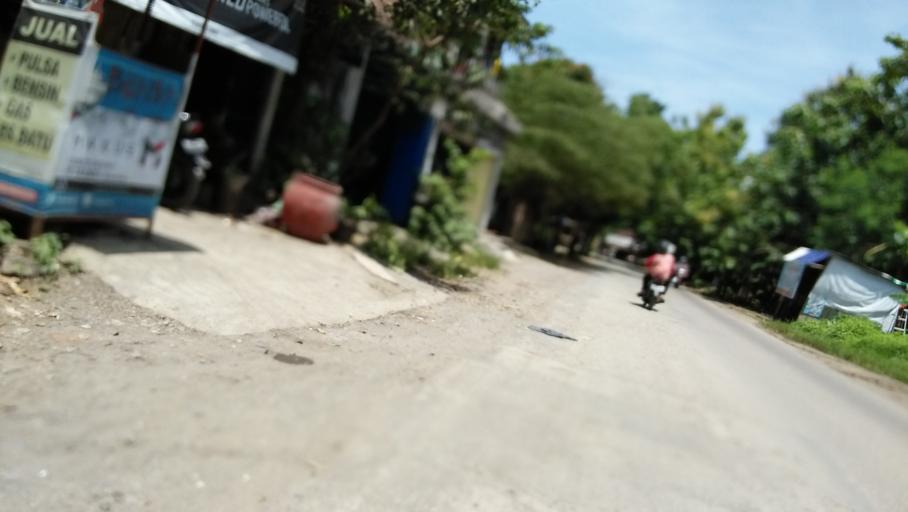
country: ID
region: Central Java
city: Mranggen
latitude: -7.0515
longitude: 110.4717
